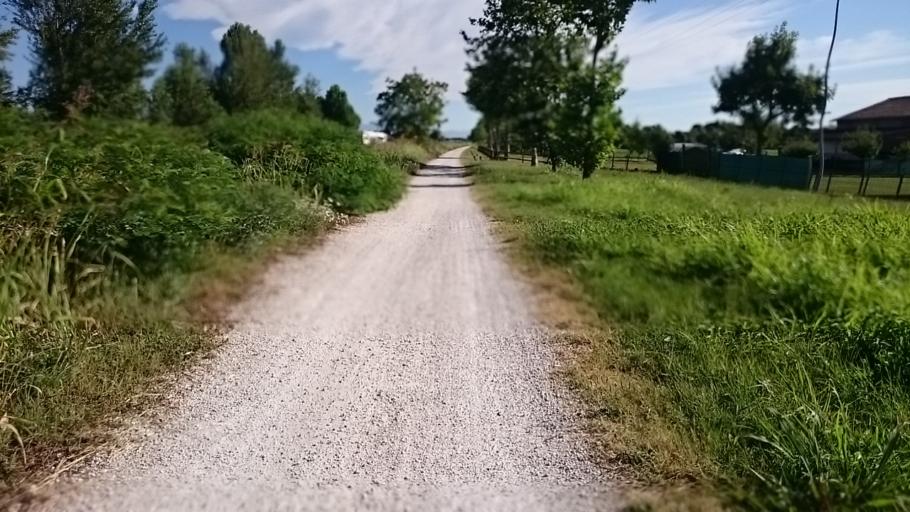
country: IT
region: Veneto
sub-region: Provincia di Padova
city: Camposampiero
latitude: 45.5481
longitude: 11.9304
